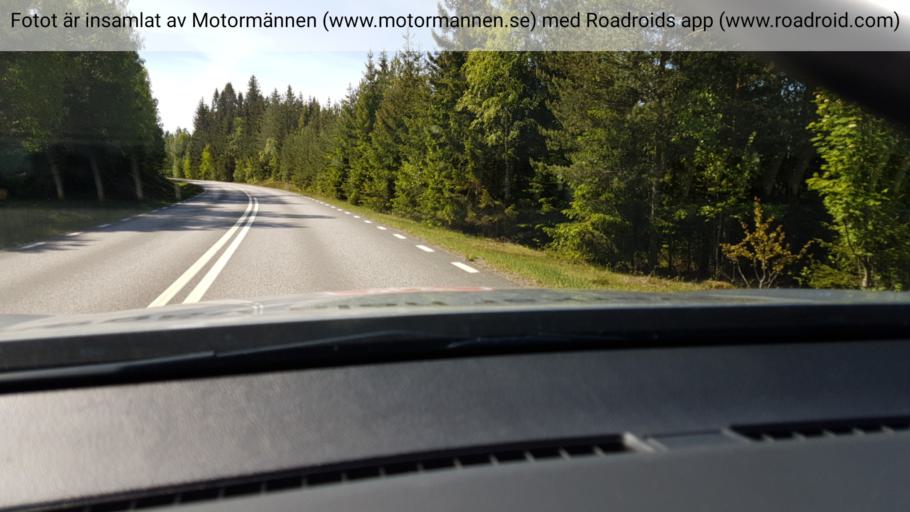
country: SE
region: Vaestra Goetaland
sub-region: Tibro Kommun
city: Tibro
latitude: 58.3789
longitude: 14.2015
